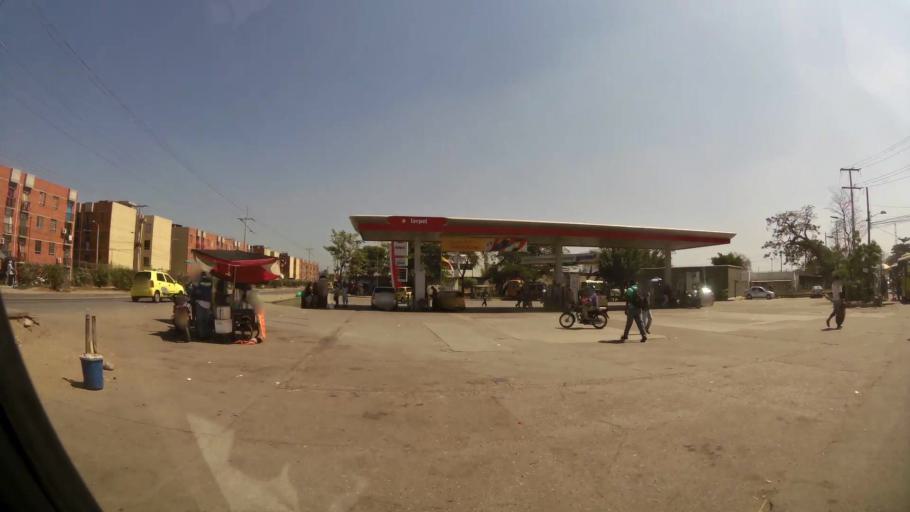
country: CO
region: Bolivar
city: Cartagena
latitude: 10.4022
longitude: -75.4601
